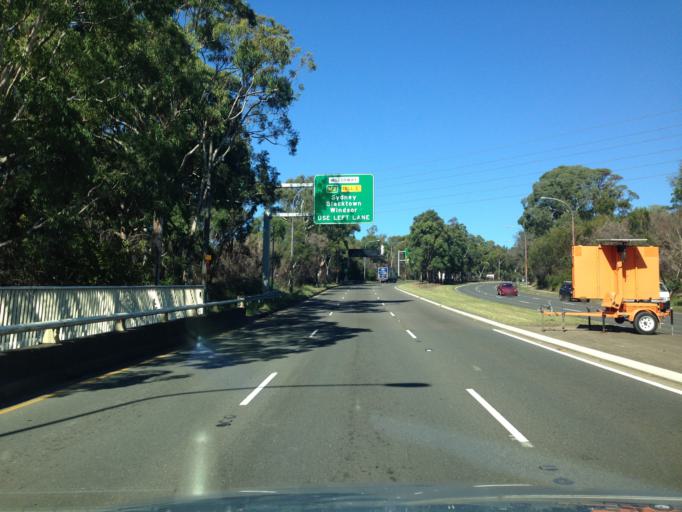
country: AU
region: New South Wales
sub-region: Ryde
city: Macquarie Park
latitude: -33.7761
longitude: 151.1355
